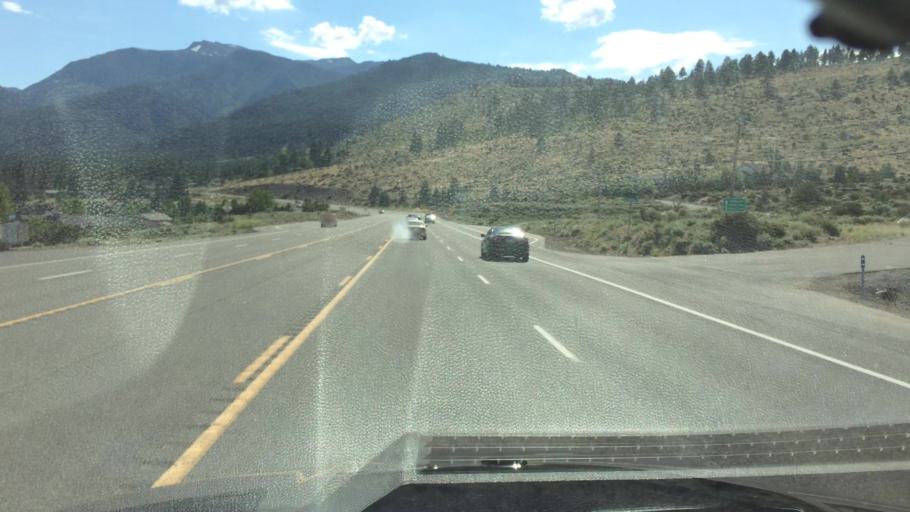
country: US
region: Nevada
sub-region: Washoe County
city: Reno
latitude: 39.3776
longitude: -119.8343
